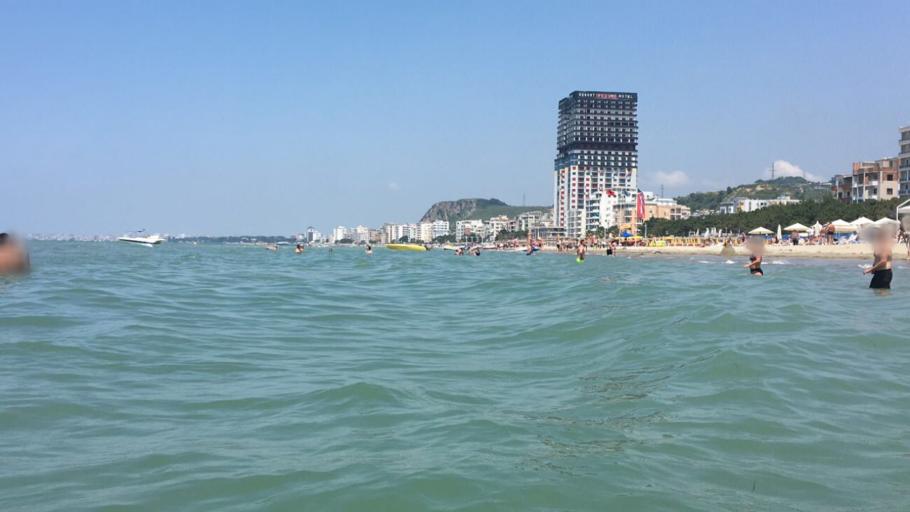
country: AL
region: Tirane
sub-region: Rrethi i Kavajes
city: Golem
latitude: 41.2704
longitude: 19.5169
